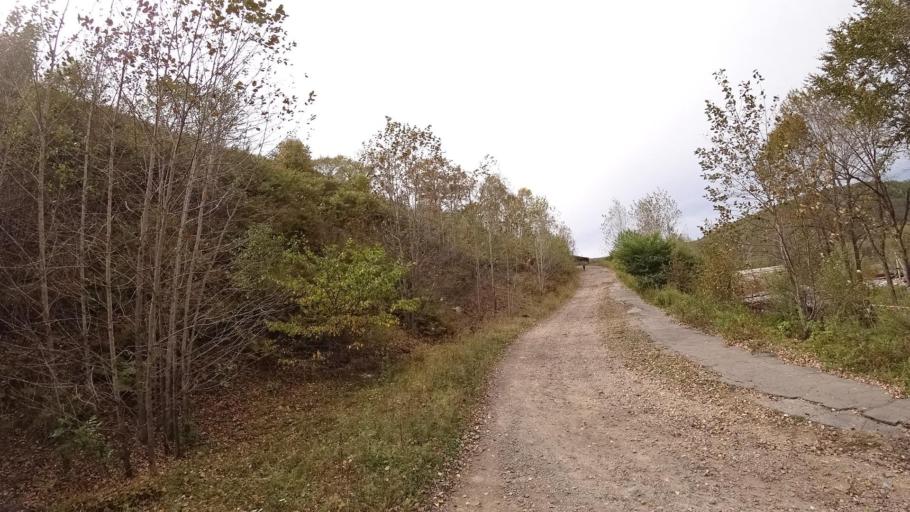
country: RU
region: Jewish Autonomous Oblast
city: Khingansk
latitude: 49.1246
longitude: 131.1974
